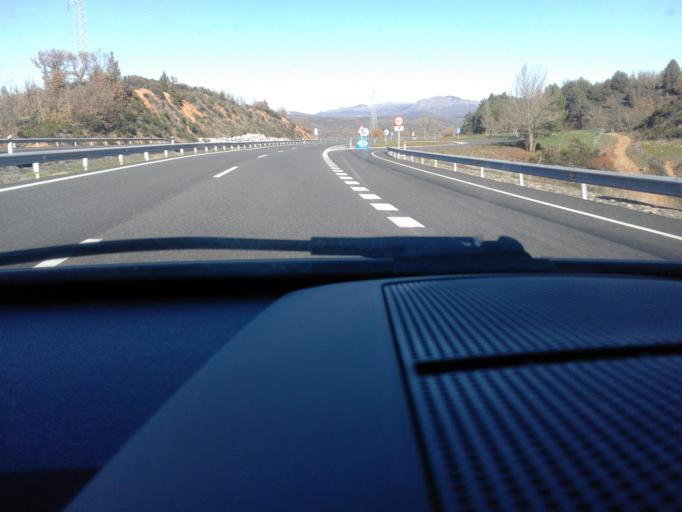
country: ES
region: Castille and Leon
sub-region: Provincia de Leon
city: Santa Maria de Ordas
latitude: 42.7109
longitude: -5.7959
